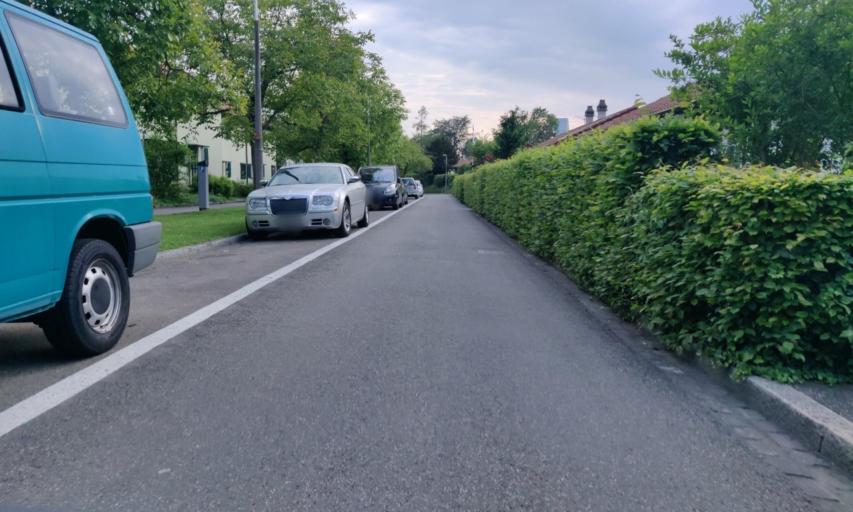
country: CH
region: Basel-Landschaft
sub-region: Bezirk Arlesheim
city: Birsfelden
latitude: 47.5668
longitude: 7.6309
